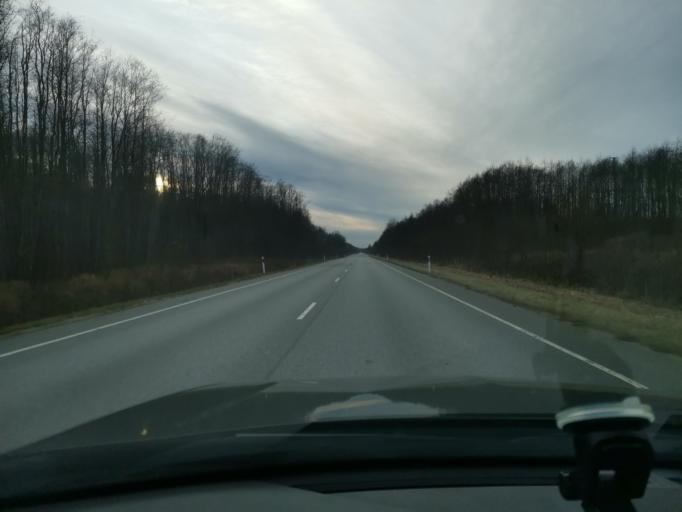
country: EE
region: Ida-Virumaa
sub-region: Narva-Joesuu linn
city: Narva-Joesuu
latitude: 59.3332
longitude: 27.9557
